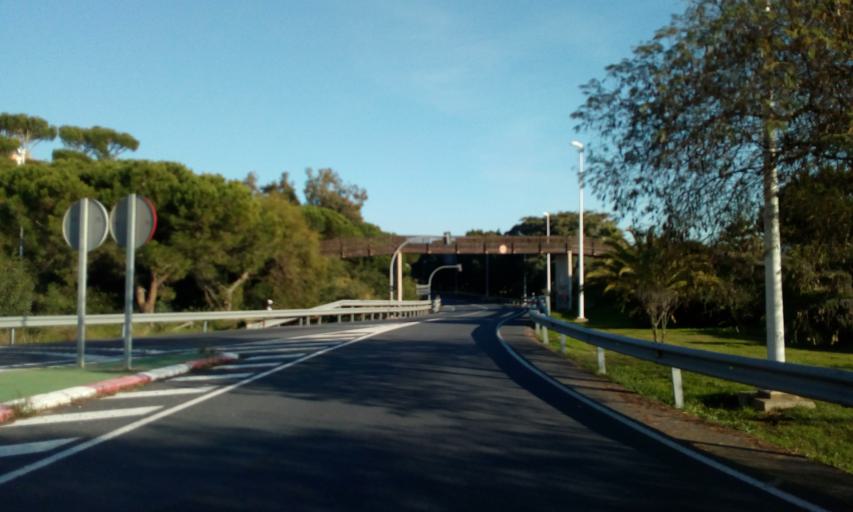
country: ES
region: Andalusia
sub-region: Provincia de Huelva
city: Lepe
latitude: 37.2086
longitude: -7.2439
